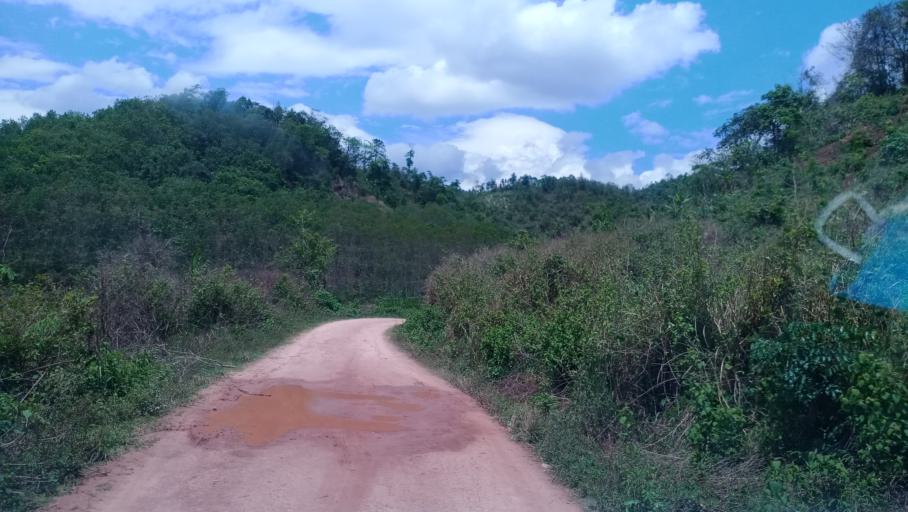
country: CN
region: Yunnan
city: Menglie
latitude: 22.1616
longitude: 101.7485
